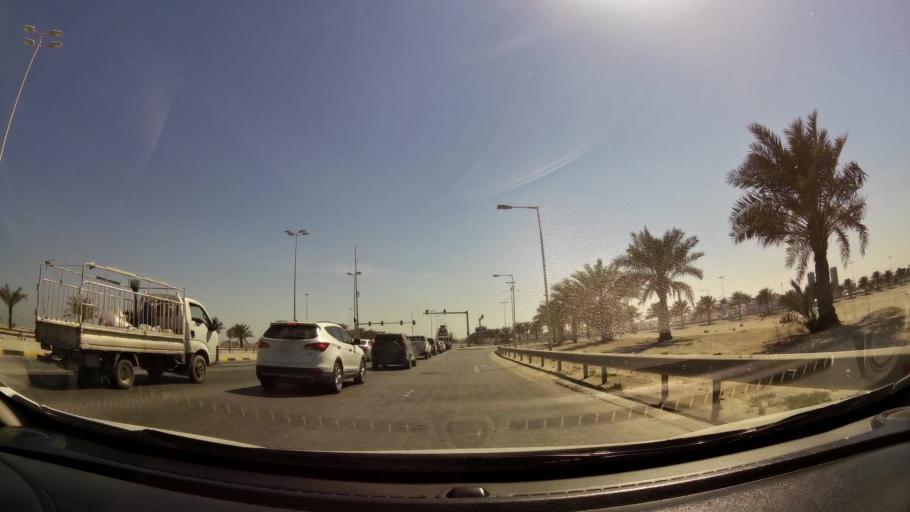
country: BH
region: Muharraq
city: Al Hadd
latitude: 26.2551
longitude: 50.6597
